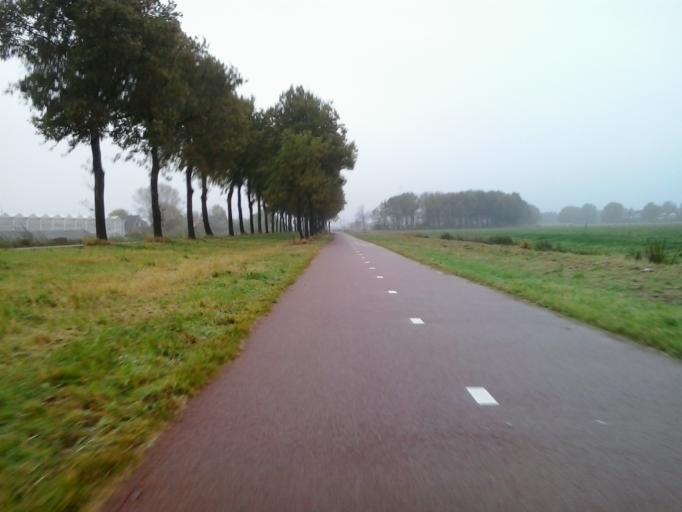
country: NL
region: South Holland
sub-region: Gemeente Lansingerland
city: Bergschenhoek
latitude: 52.0093
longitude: 4.5024
